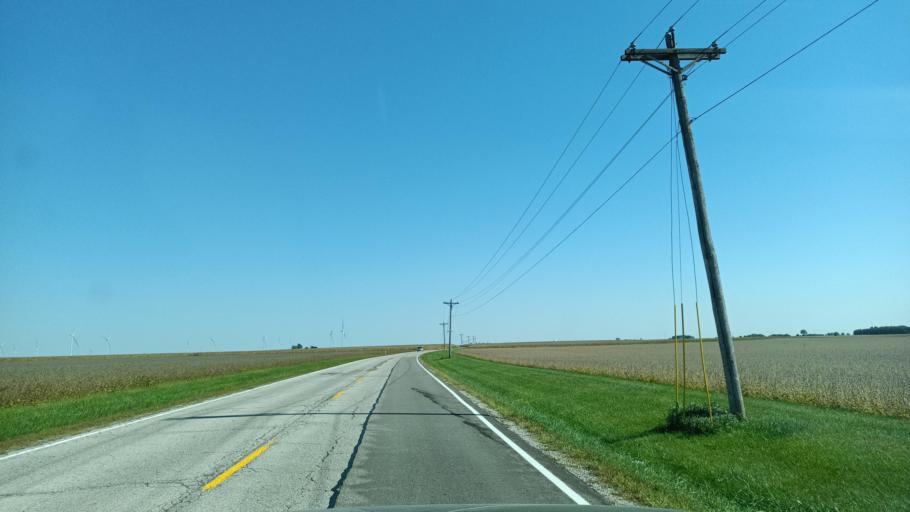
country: US
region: Illinois
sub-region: McLean County
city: Le Roy
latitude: 40.3215
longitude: -88.7153
